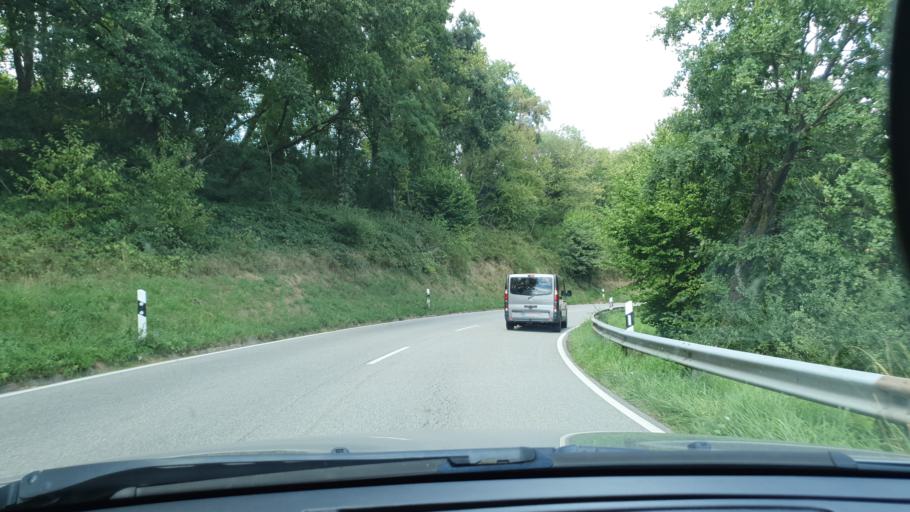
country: DE
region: Rheinland-Pfalz
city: Hohfroschen
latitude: 49.2532
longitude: 7.5714
